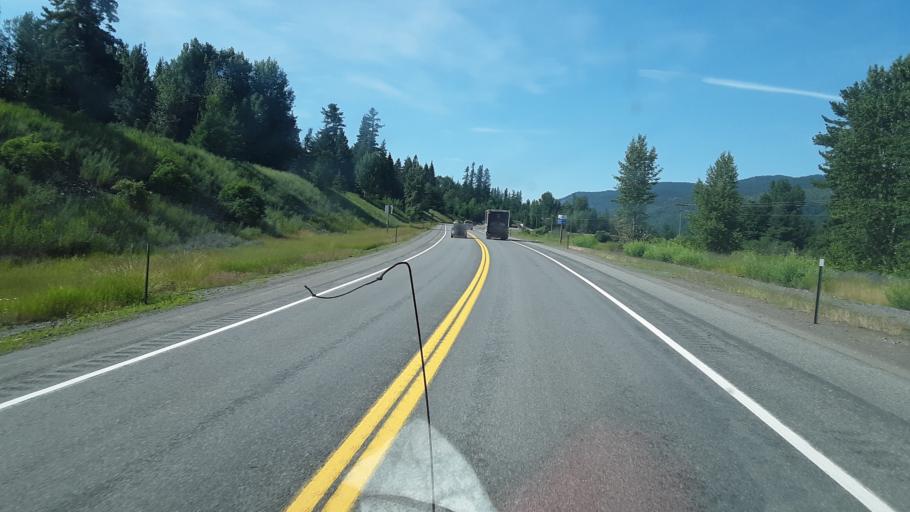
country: US
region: Idaho
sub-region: Bonner County
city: Ponderay
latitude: 48.4048
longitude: -116.5284
